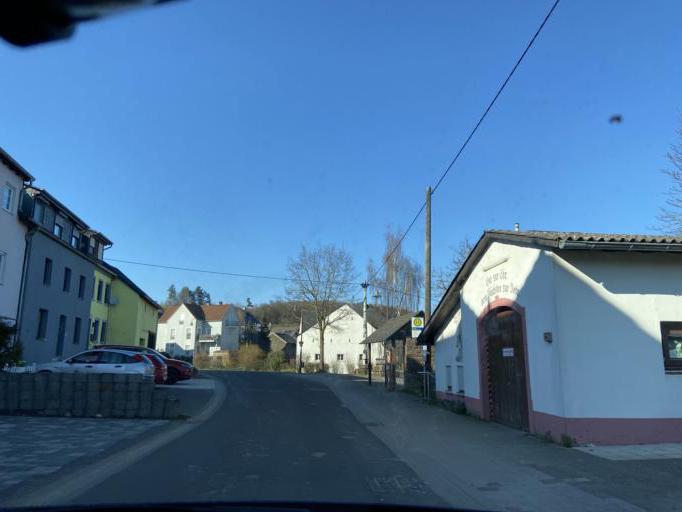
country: DE
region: Rheinland-Pfalz
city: Aach
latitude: 49.8013
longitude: 6.6023
